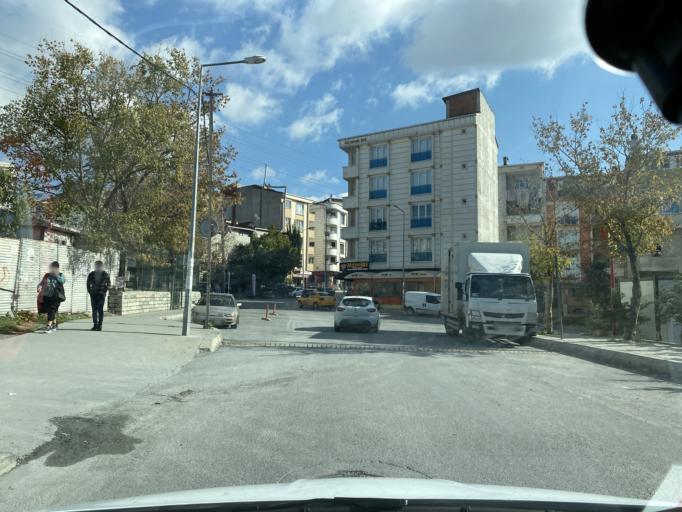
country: TR
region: Istanbul
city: Esenyurt
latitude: 41.0275
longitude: 28.6707
